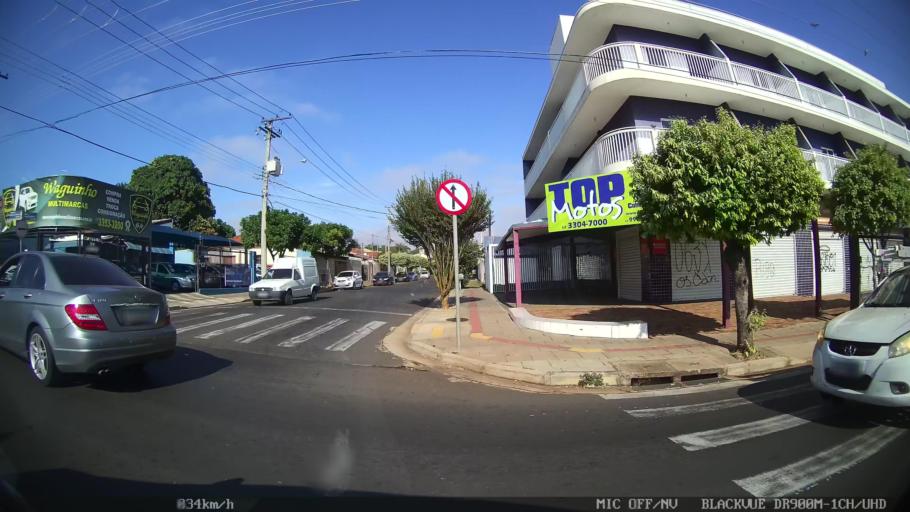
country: BR
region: Sao Paulo
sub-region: Sao Jose Do Rio Preto
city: Sao Jose do Rio Preto
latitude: -20.8054
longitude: -49.4037
